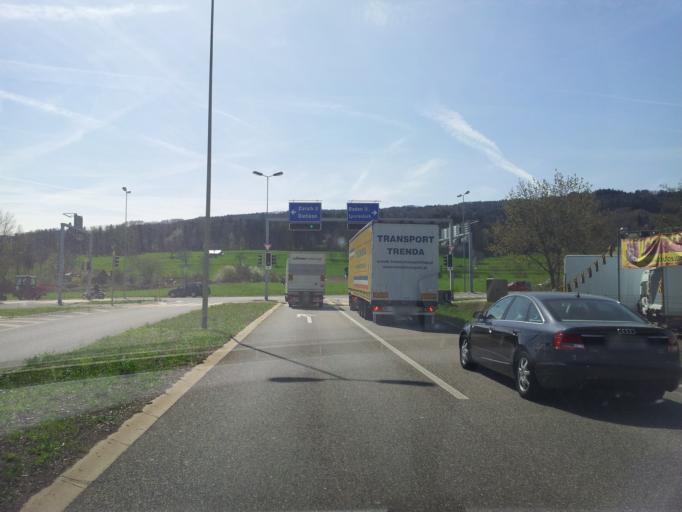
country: CH
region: Zurich
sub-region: Bezirk Dietikon
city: Dietikon / Almend
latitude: 47.4130
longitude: 8.3839
